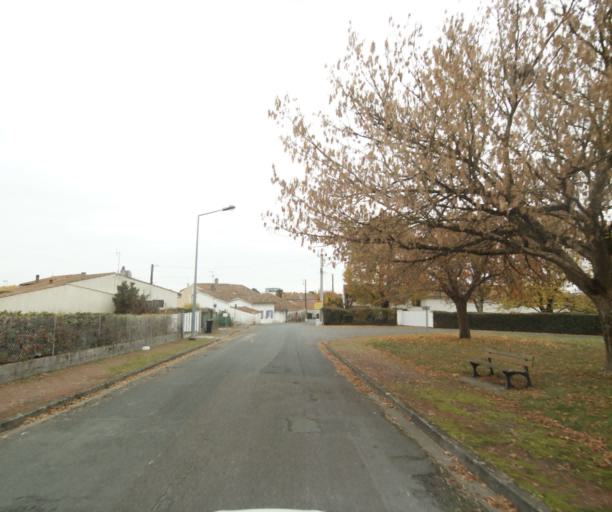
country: FR
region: Poitou-Charentes
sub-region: Departement de la Charente-Maritime
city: Saintes
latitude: 45.7299
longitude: -0.6424
